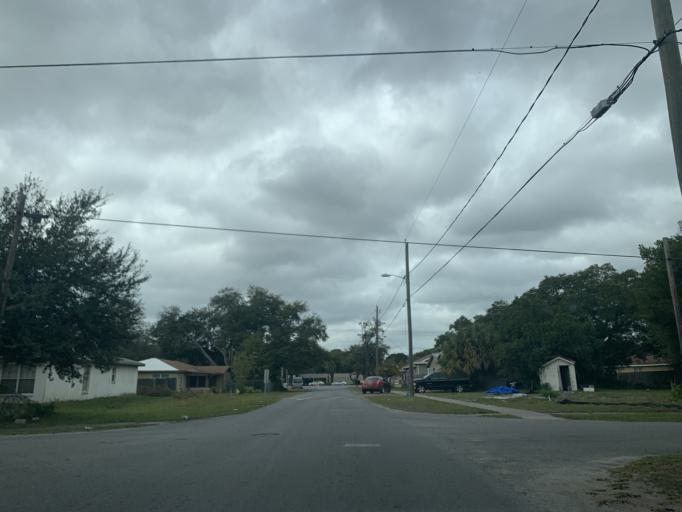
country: US
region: Florida
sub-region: Hillsborough County
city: East Lake-Orient Park
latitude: 27.9779
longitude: -82.4000
